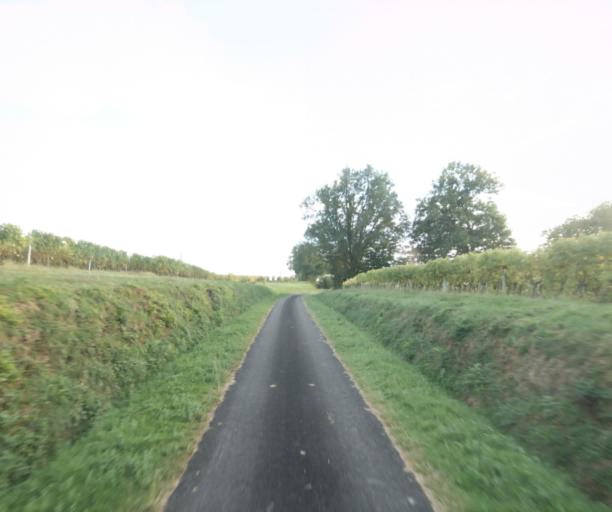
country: FR
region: Midi-Pyrenees
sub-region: Departement du Gers
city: Le Houga
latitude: 43.8447
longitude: -0.1129
